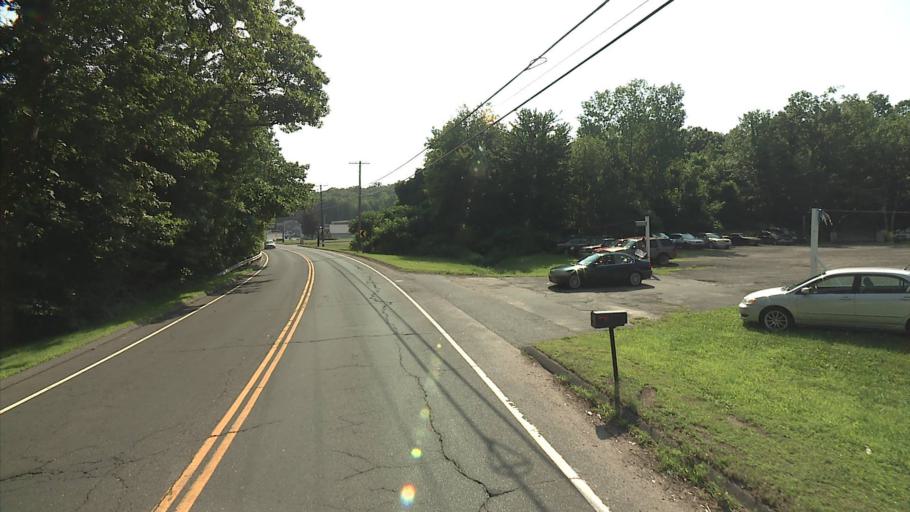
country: US
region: Connecticut
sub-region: New Haven County
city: Wolcott
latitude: 41.5559
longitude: -72.9524
